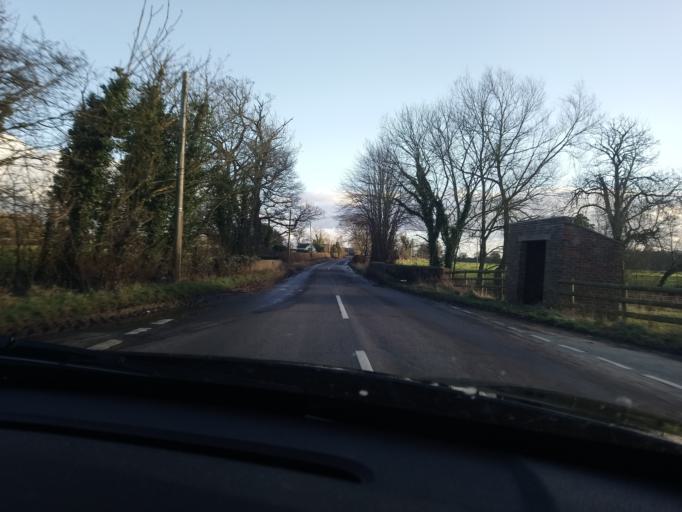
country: GB
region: England
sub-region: Shropshire
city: Petton
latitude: 52.8762
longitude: -2.7829
